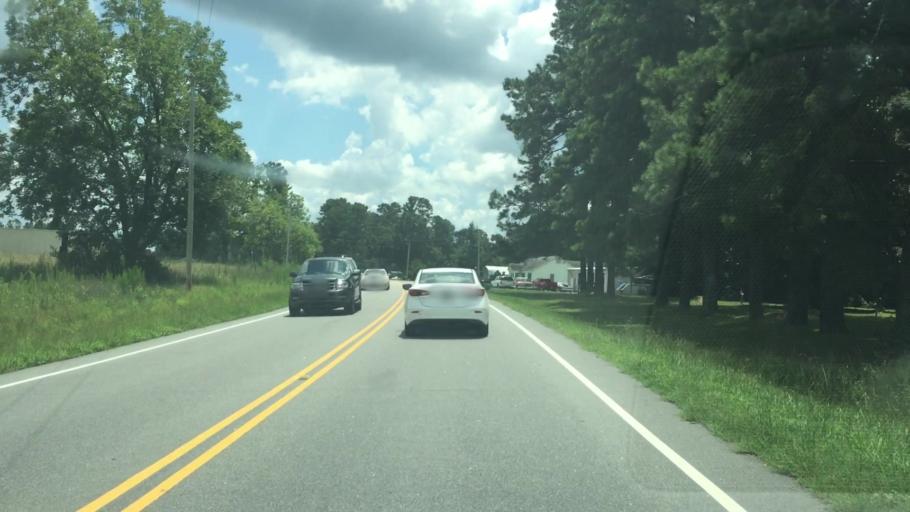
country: US
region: North Carolina
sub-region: Columbus County
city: Chadbourn
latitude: 34.2927
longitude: -78.8260
